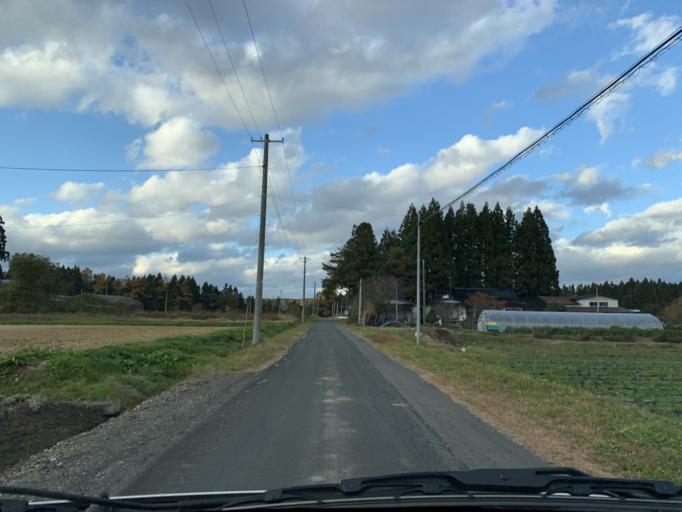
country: JP
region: Iwate
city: Mizusawa
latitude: 39.1139
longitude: 141.0234
